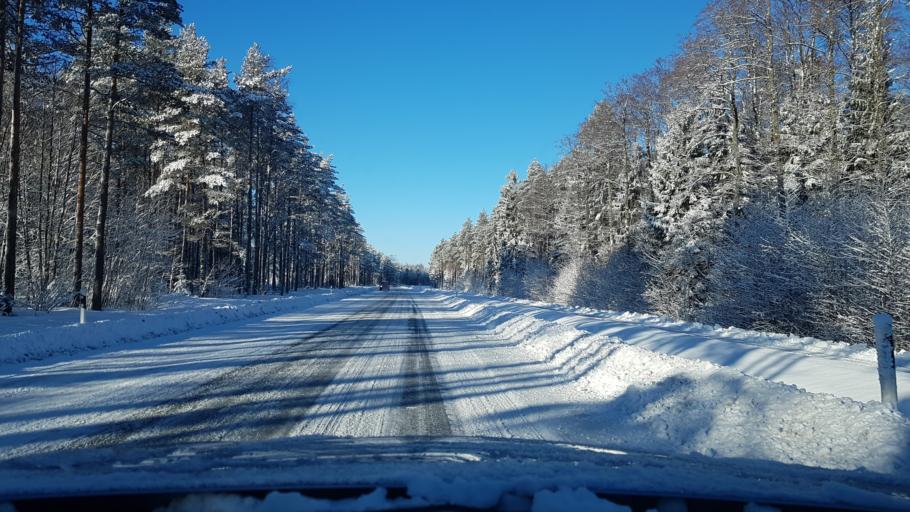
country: EE
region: Hiiumaa
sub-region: Kaerdla linn
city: Kardla
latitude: 58.9957
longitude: 22.7168
